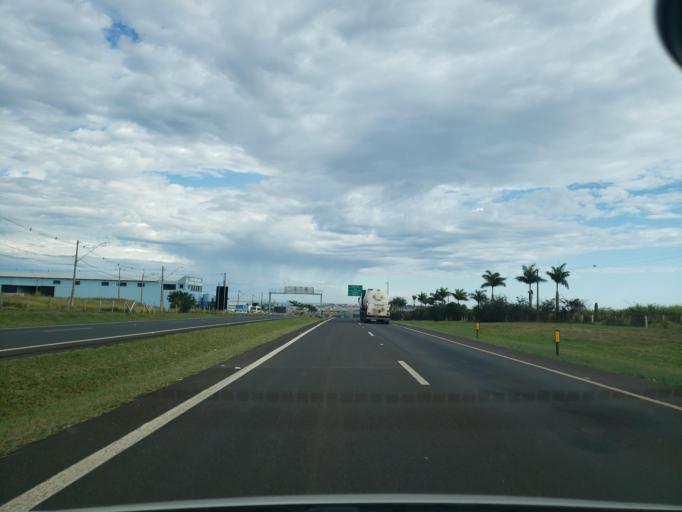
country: BR
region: Sao Paulo
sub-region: Jau
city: Jau
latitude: -22.2664
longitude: -48.5084
